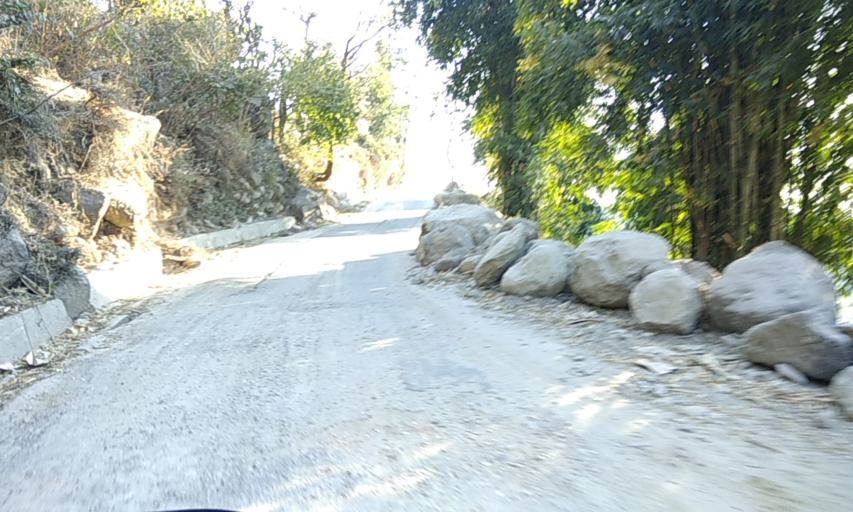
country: IN
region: Himachal Pradesh
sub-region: Kangra
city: Palampur
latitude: 32.1348
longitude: 76.5353
